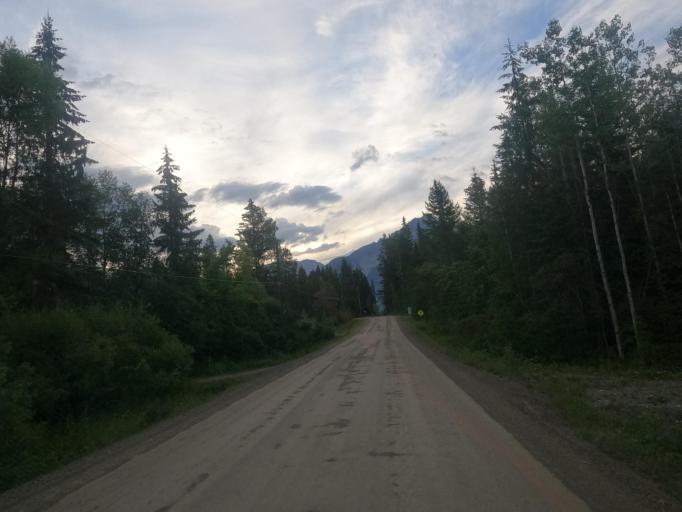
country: CA
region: British Columbia
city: Golden
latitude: 51.4384
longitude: -117.0434
